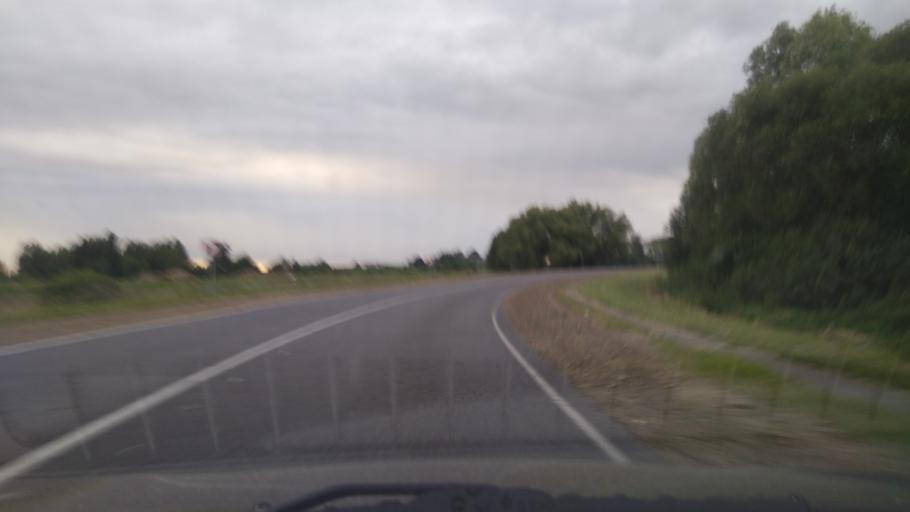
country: BY
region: Brest
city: Byaroza
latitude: 52.4171
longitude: 24.9804
